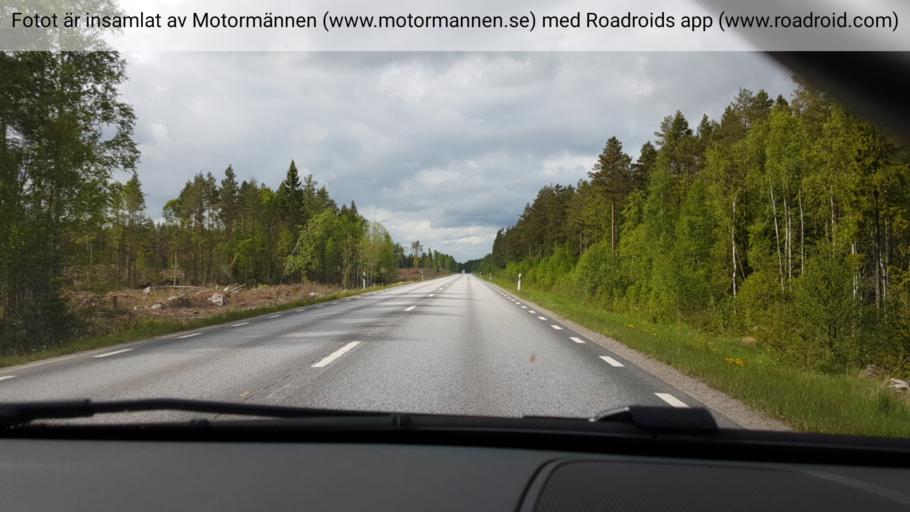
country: SE
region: Uppsala
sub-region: Tierps Kommun
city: Tierp
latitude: 60.3061
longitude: 17.5583
